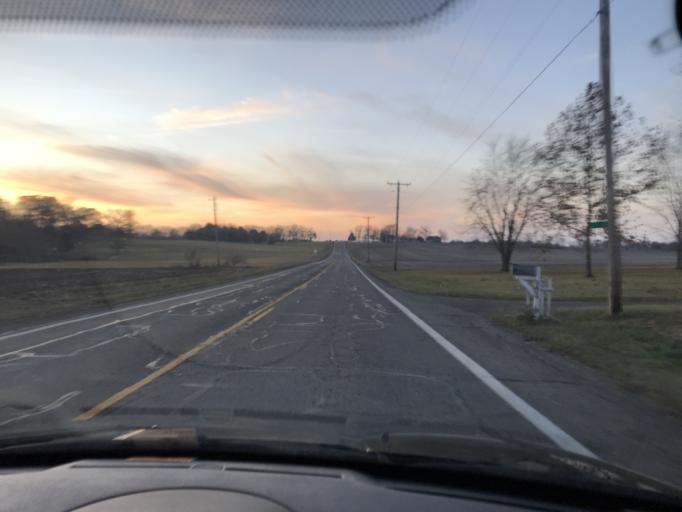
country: US
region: Ohio
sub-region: Champaign County
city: Urbana
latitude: 40.1082
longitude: -83.6964
